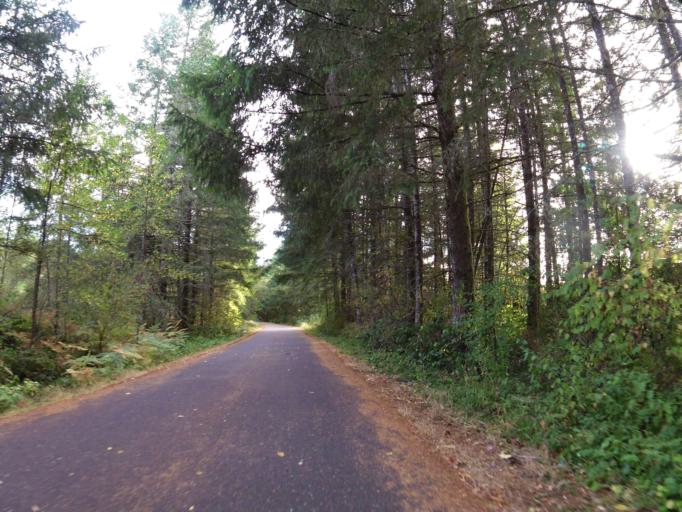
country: US
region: Washington
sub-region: Thurston County
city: Lacey
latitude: 46.9440
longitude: -122.8201
